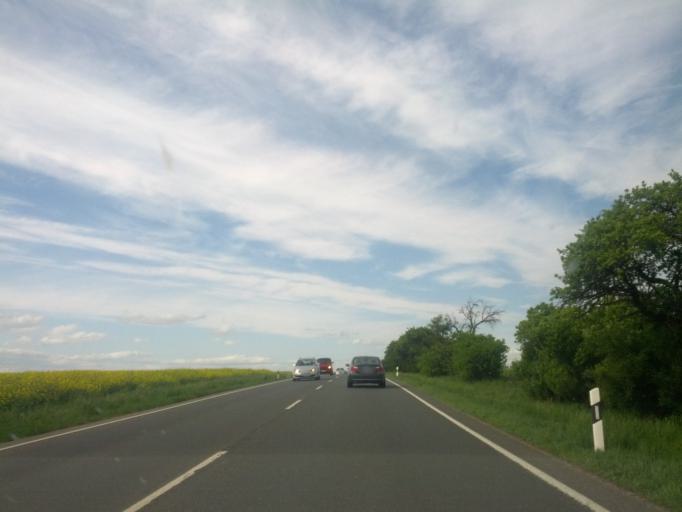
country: DE
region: Thuringia
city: Rockhausen
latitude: 50.9229
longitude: 11.0387
